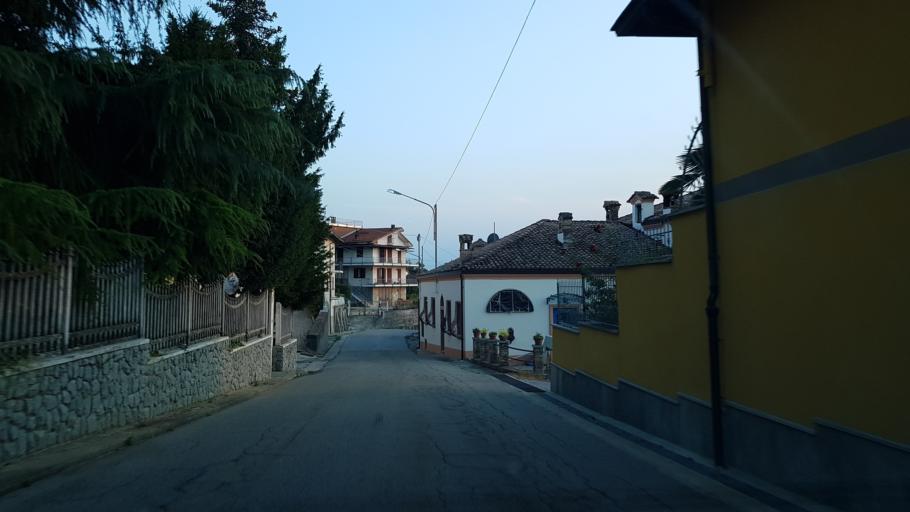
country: IT
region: Piedmont
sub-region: Provincia di Cuneo
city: Novello
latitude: 44.5880
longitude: 7.9264
